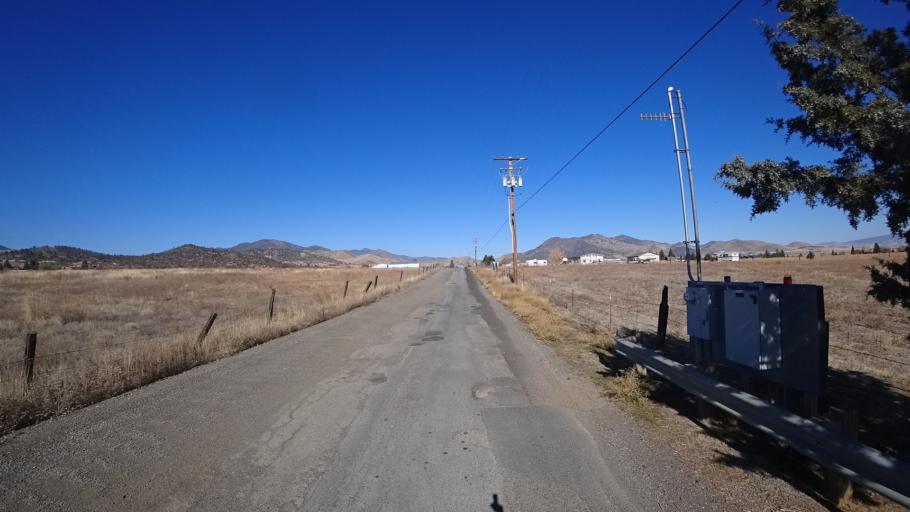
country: US
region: California
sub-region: Siskiyou County
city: Yreka
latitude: 41.7394
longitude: -122.5933
